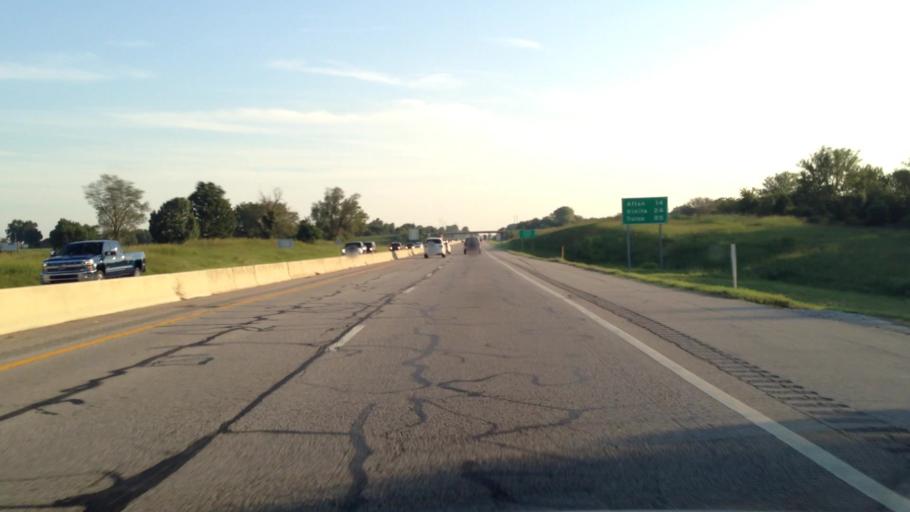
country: US
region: Oklahoma
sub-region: Ottawa County
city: Miami
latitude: 36.8506
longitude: -94.8568
